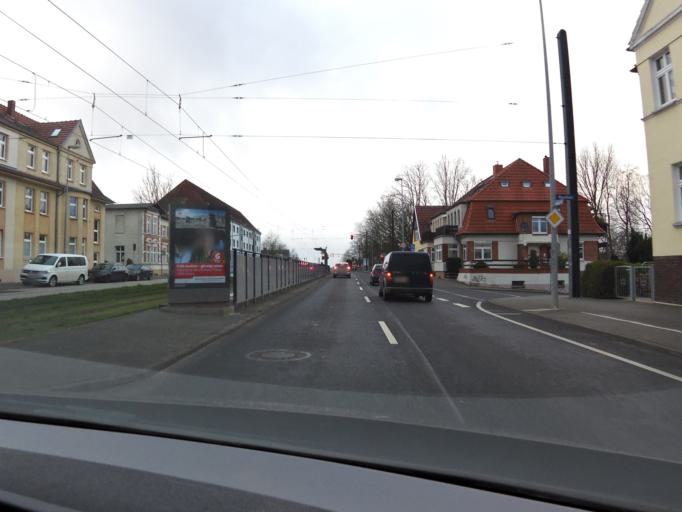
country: DE
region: Mecklenburg-Vorpommern
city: Weststadt
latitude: 53.6410
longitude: 11.3911
